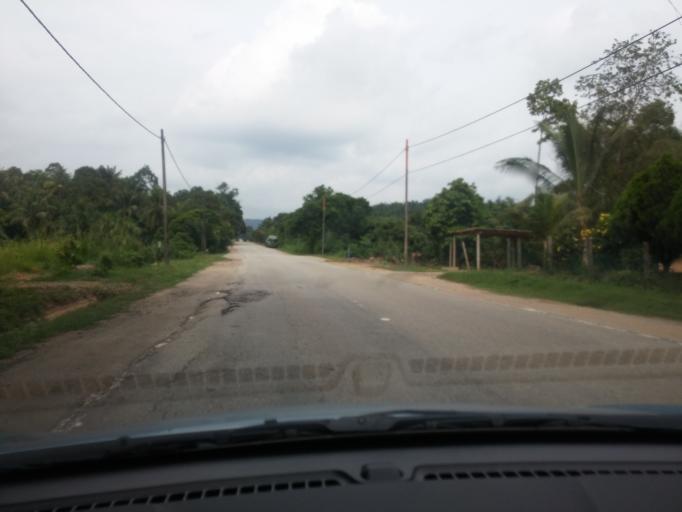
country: MY
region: Pahang
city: Kuantan
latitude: 3.8840
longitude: 103.1603
